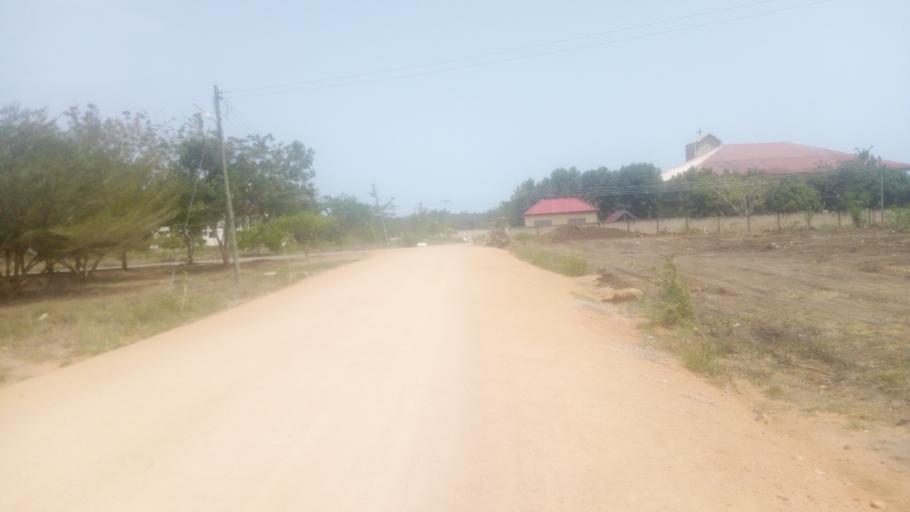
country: GH
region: Central
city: Winneba
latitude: 5.3690
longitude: -0.6303
